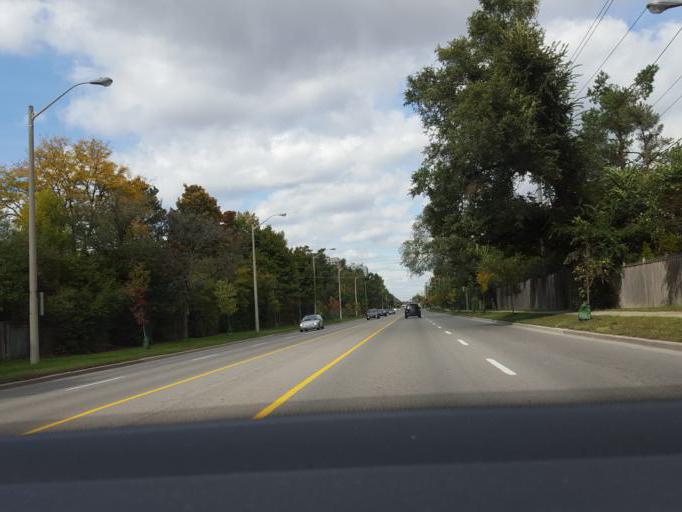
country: CA
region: Ontario
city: Willowdale
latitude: 43.7472
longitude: -79.3588
